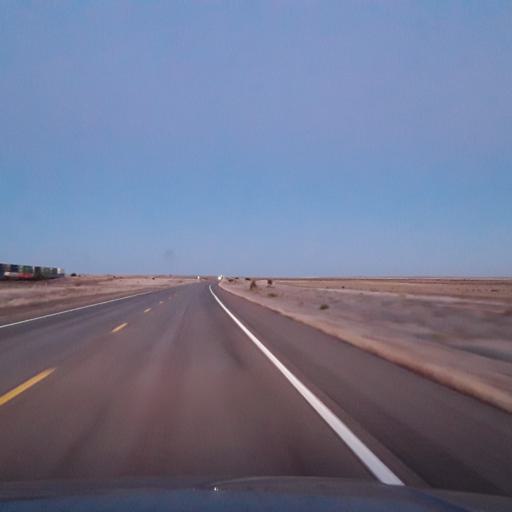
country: US
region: New Mexico
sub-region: Guadalupe County
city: Santa Rosa
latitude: 34.7544
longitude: -105.0030
